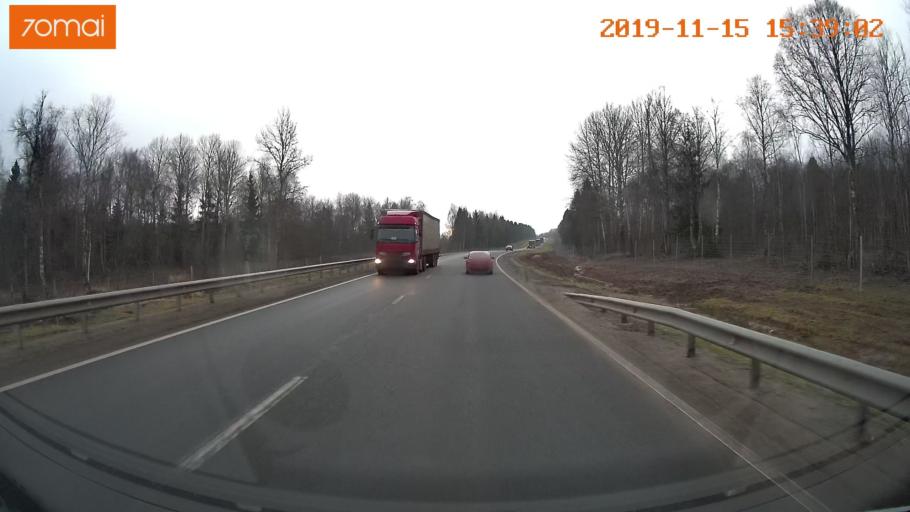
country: RU
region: Jaroslavl
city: Danilov
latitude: 58.0245
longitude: 40.0737
